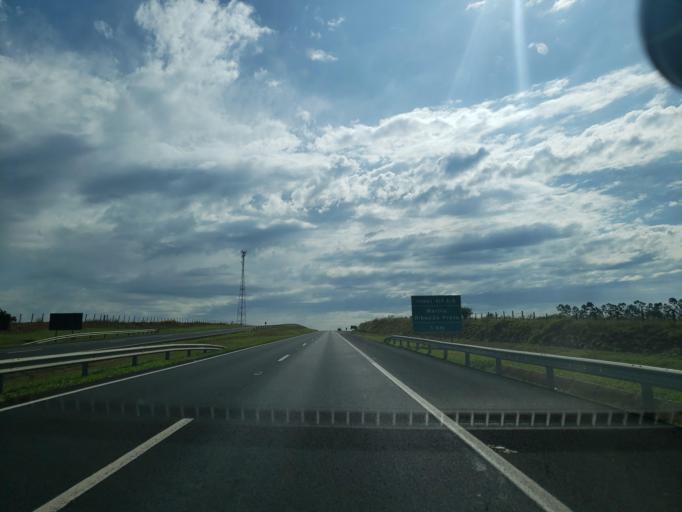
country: BR
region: Sao Paulo
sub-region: Cafelandia
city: Cafelandia
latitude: -21.8851
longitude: -49.5485
